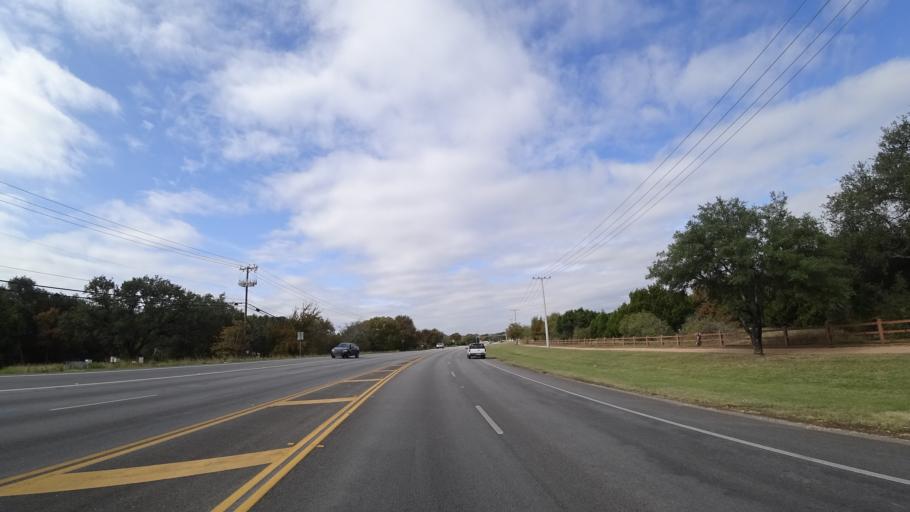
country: US
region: Texas
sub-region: Williamson County
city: Brushy Creek
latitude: 30.5303
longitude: -97.7201
